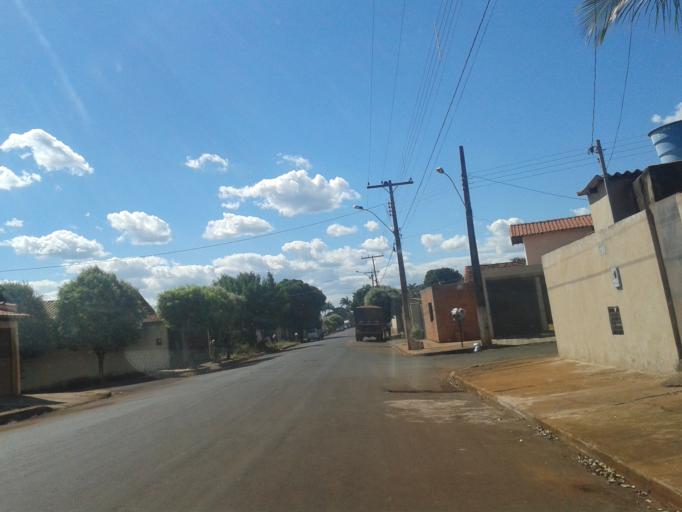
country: BR
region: Minas Gerais
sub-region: Capinopolis
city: Capinopolis
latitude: -18.6914
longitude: -49.5688
